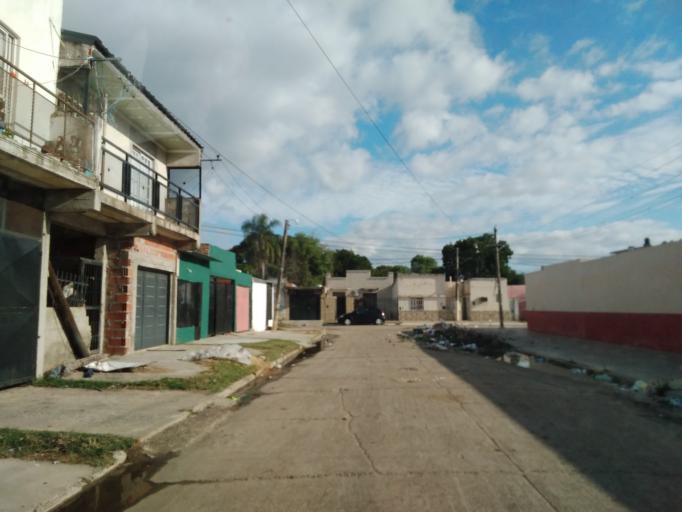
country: AR
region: Corrientes
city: Corrientes
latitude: -27.4614
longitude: -58.8174
